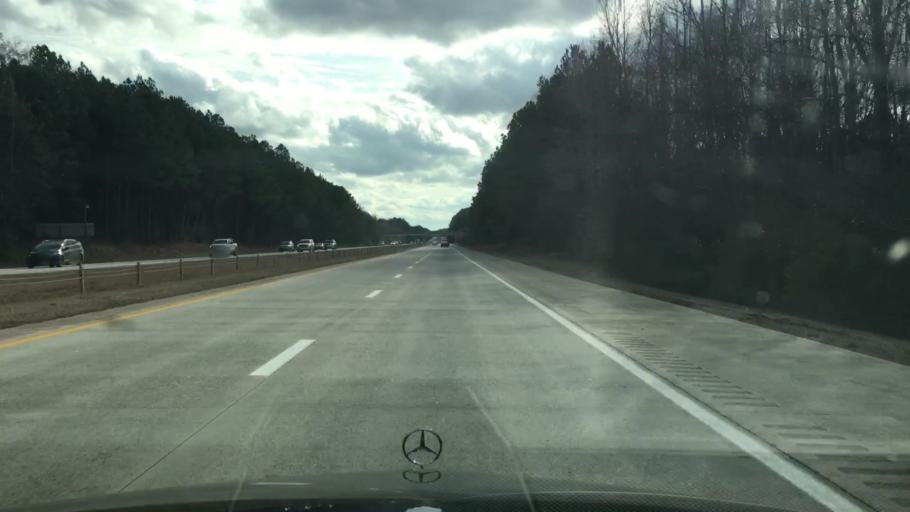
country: US
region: North Carolina
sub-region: Johnston County
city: Benson
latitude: 35.4953
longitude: -78.5533
